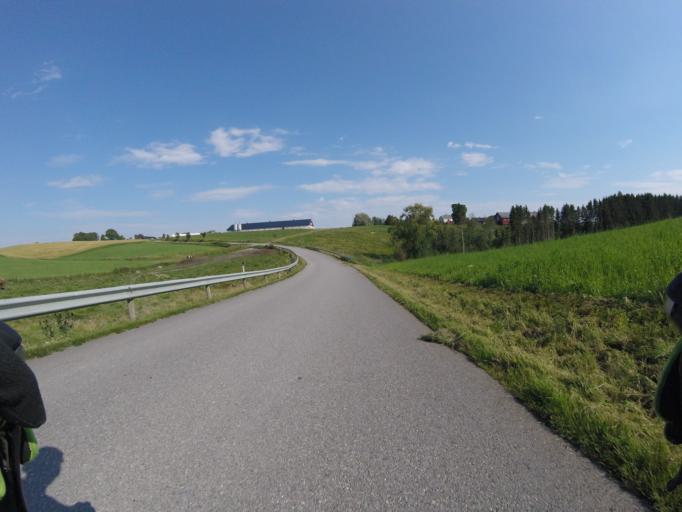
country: NO
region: Akershus
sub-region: Ullensaker
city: Klofta
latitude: 60.0963
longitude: 11.1706
